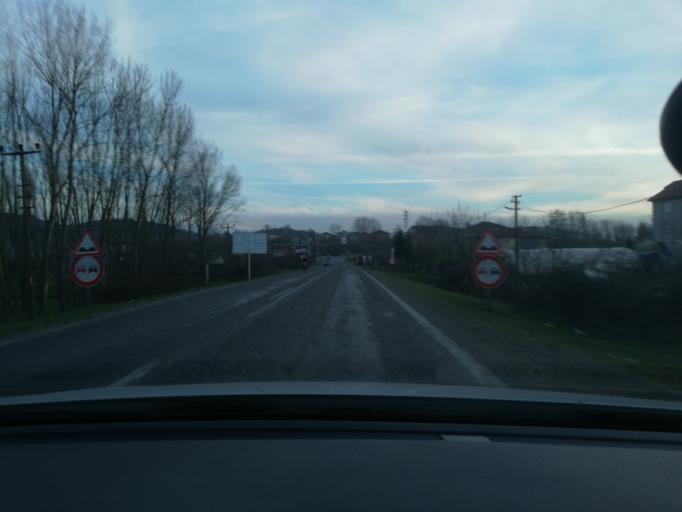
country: TR
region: Zonguldak
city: Saltukova
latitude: 41.5034
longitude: 32.0982
